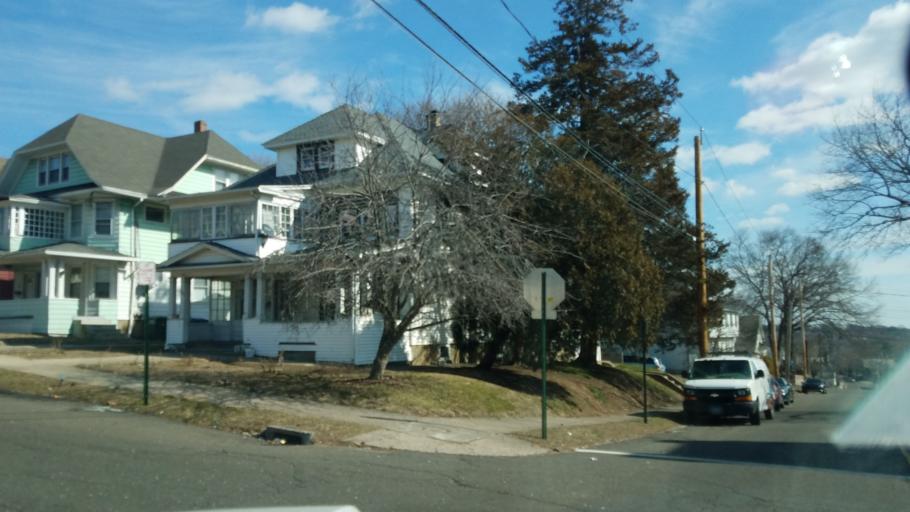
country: US
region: Connecticut
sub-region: Fairfield County
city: Stratford
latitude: 41.1919
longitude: -73.1641
